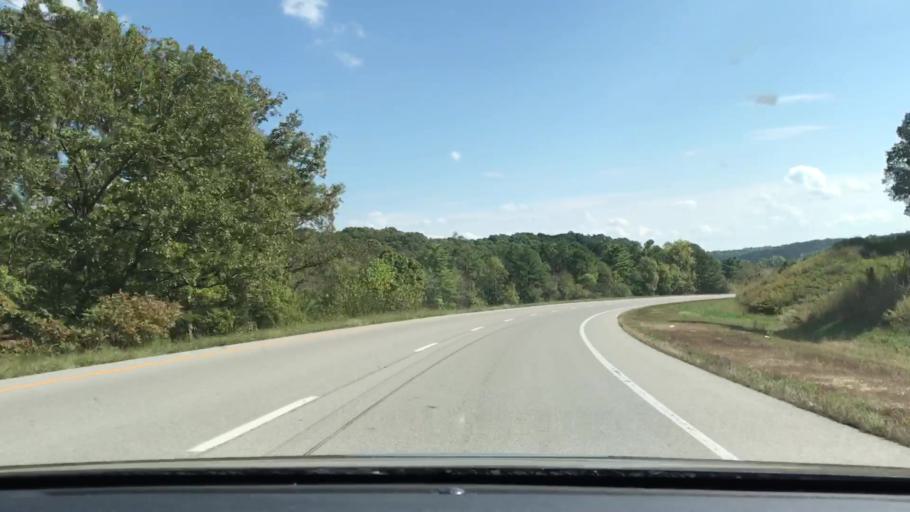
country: US
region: Kentucky
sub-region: Trigg County
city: Cadiz
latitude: 36.7863
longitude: -88.0289
